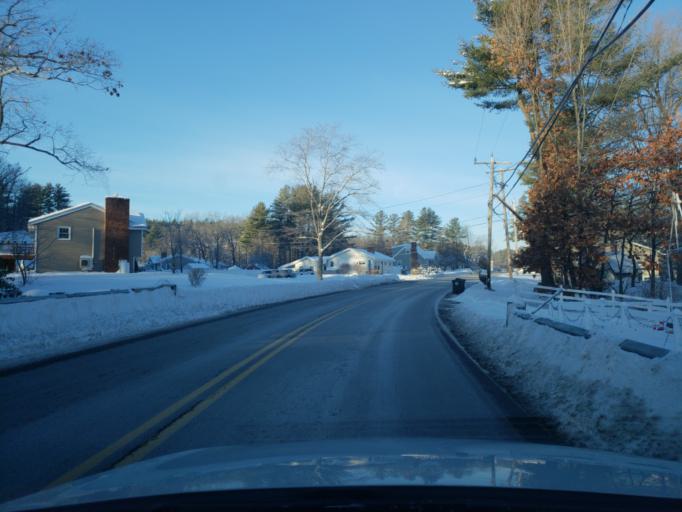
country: US
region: New Hampshire
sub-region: Hillsborough County
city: Goffstown
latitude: 43.0154
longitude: -71.6104
